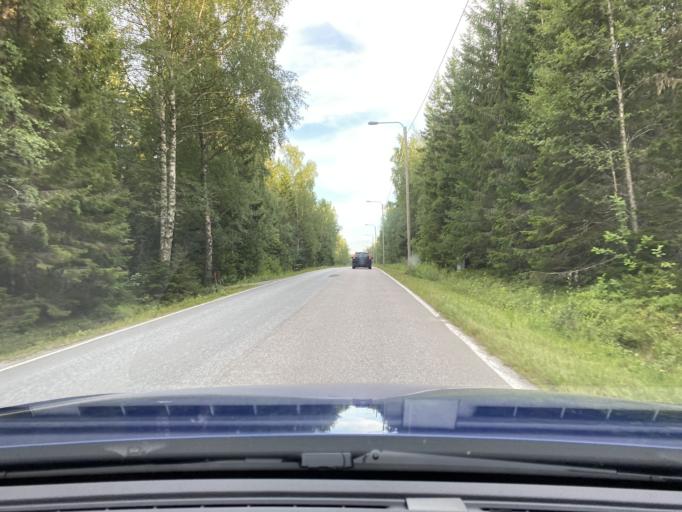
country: FI
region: Ostrobothnia
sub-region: Vaasa
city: Korsnaes
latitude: 62.9499
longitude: 21.1761
